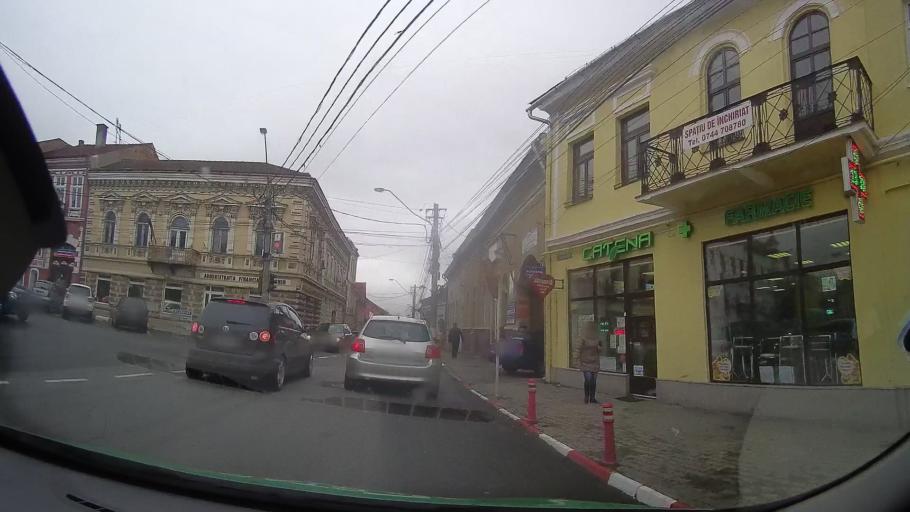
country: RO
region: Mures
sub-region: Municipiul Reghin
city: Reghin
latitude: 46.7822
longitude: 24.7019
